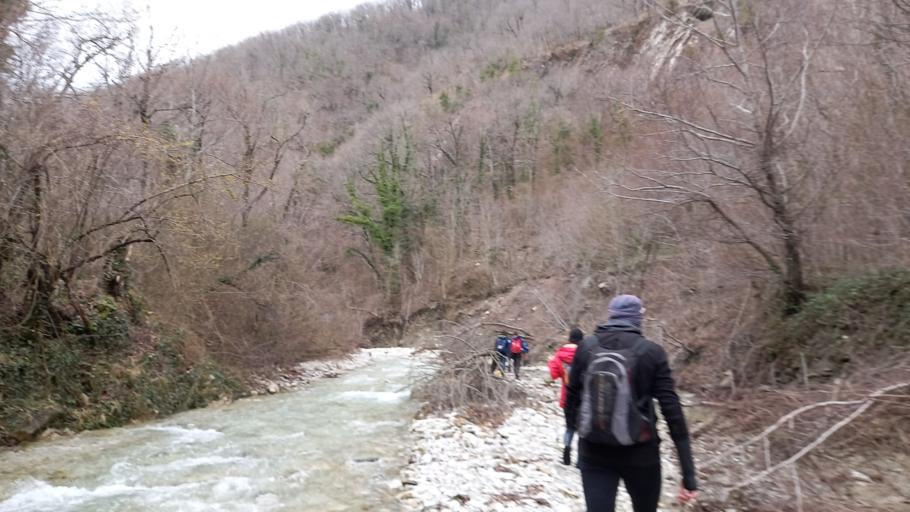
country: RU
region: Krasnodarskiy
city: Dzhubga
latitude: 44.4056
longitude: 38.7120
